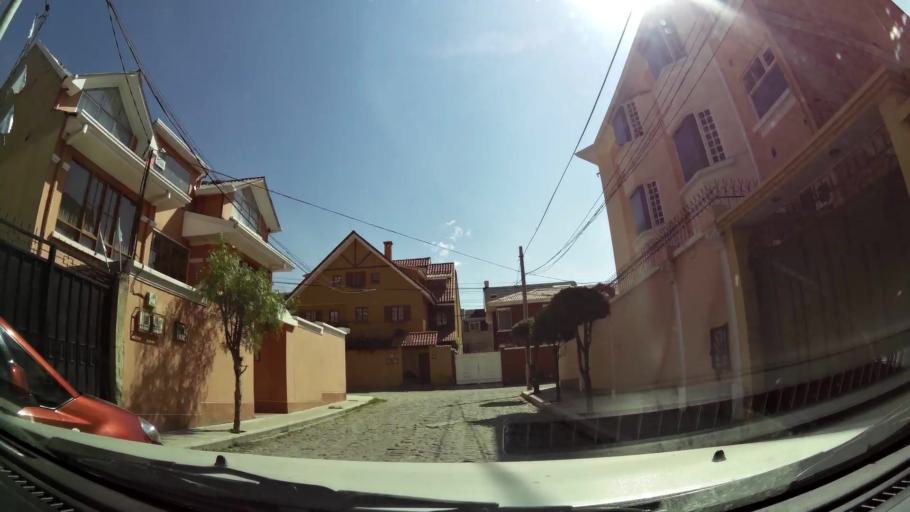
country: BO
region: La Paz
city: La Paz
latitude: -16.5212
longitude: -68.0883
